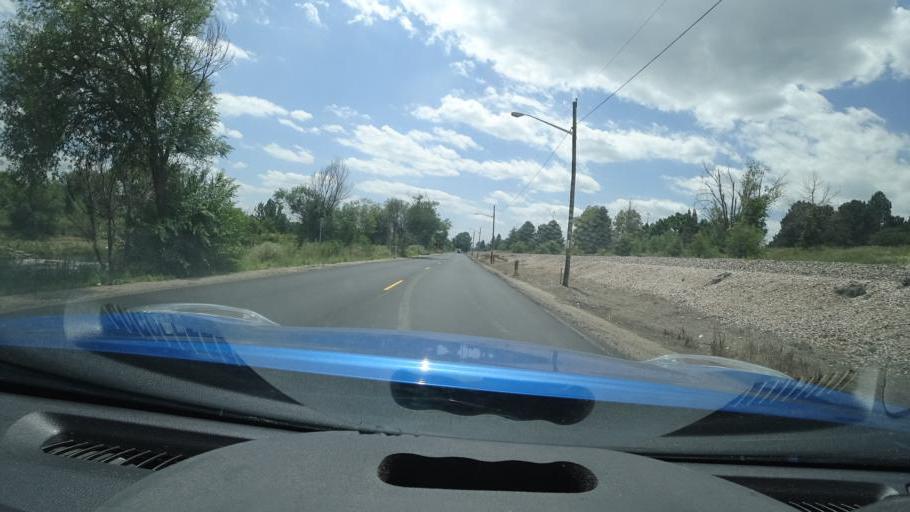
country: US
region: Colorado
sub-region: Arapahoe County
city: Englewood
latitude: 39.6873
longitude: -105.0007
